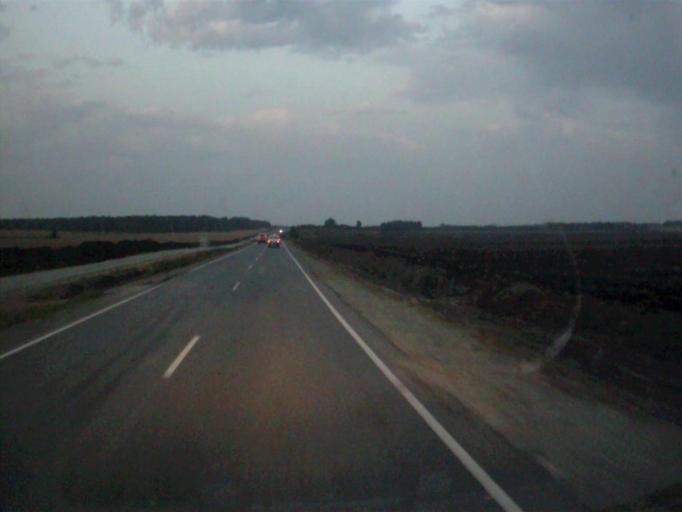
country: RU
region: Chelyabinsk
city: Timiryazevskiy
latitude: 55.2076
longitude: 60.8115
